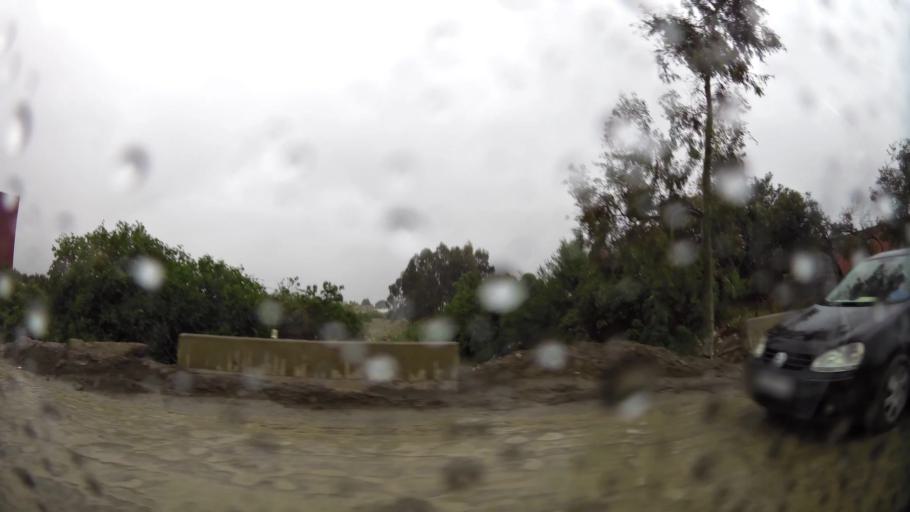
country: MA
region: Oriental
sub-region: Nador
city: Midar
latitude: 34.8760
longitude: -3.7259
